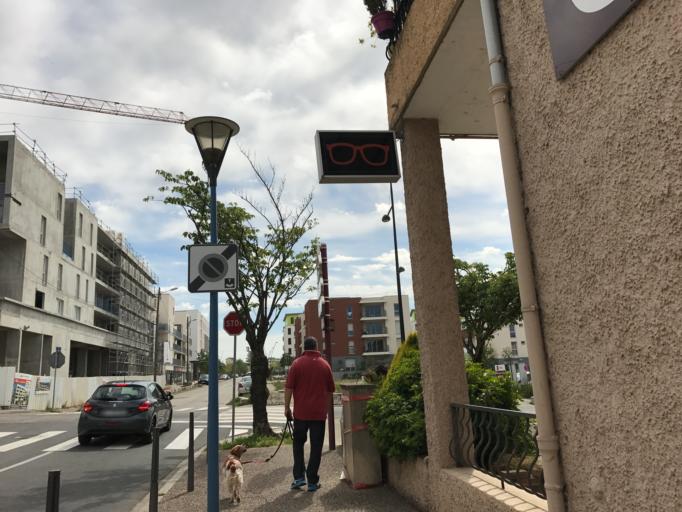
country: FR
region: Rhone-Alpes
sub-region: Departement du Rhone
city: Sathonay-Camp
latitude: 45.8253
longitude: 4.8734
